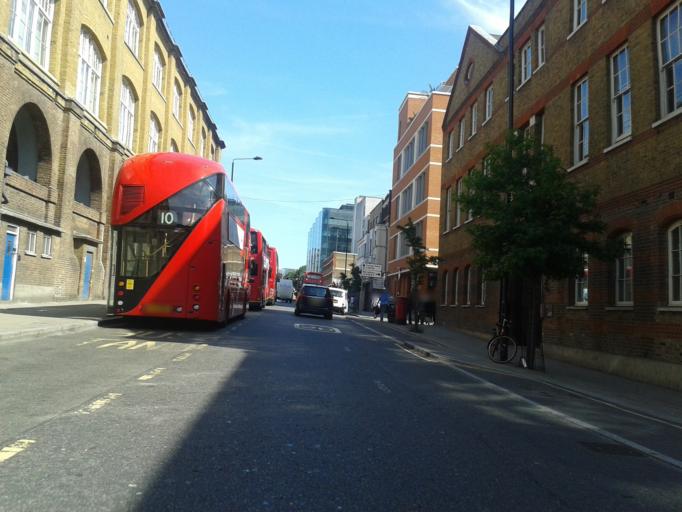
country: GB
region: England
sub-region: Greater London
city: Barnsbury
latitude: 51.5324
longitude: -0.1224
